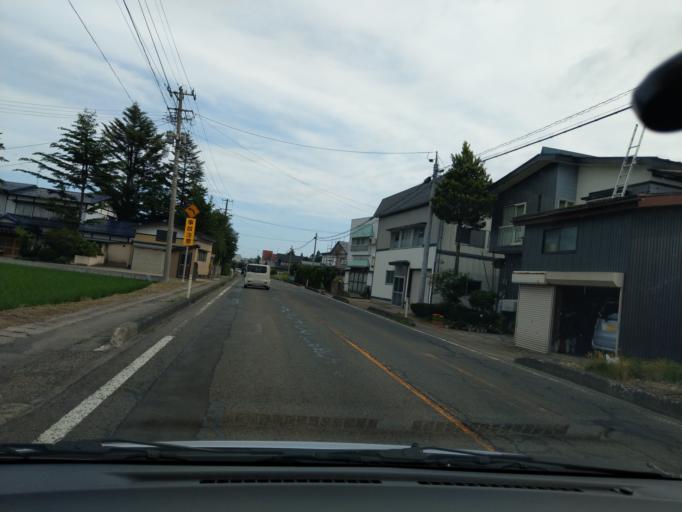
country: JP
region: Akita
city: Yokotemachi
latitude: 39.3981
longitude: 140.5640
